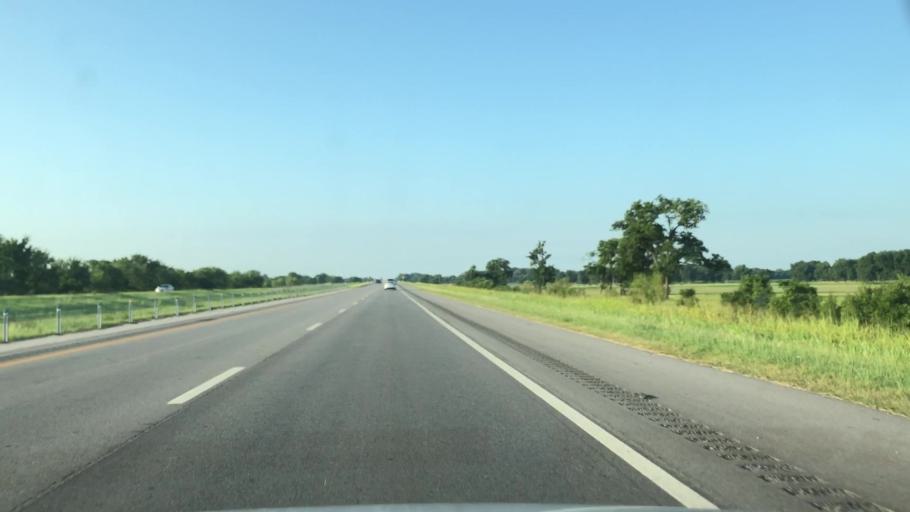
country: US
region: Oklahoma
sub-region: Washington County
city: Bartlesville
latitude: 36.6607
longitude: -95.9355
